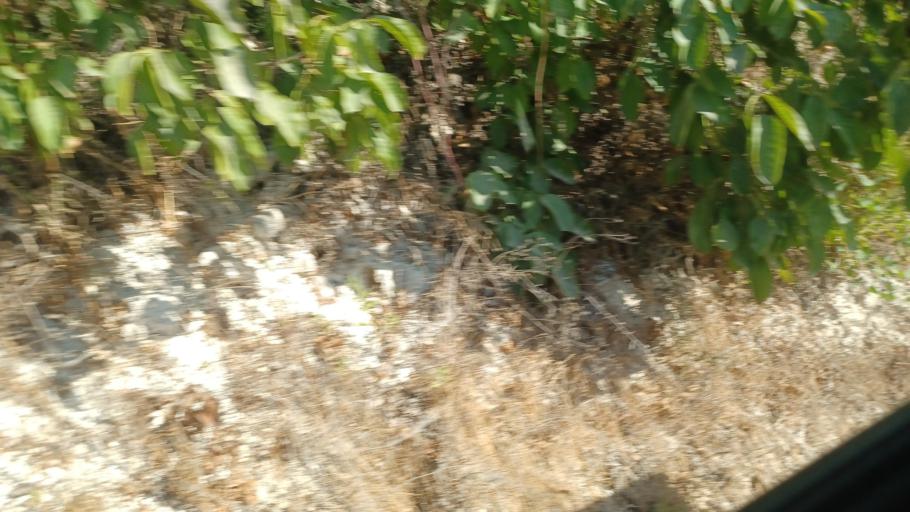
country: CY
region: Pafos
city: Mesogi
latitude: 34.8441
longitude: 32.4805
